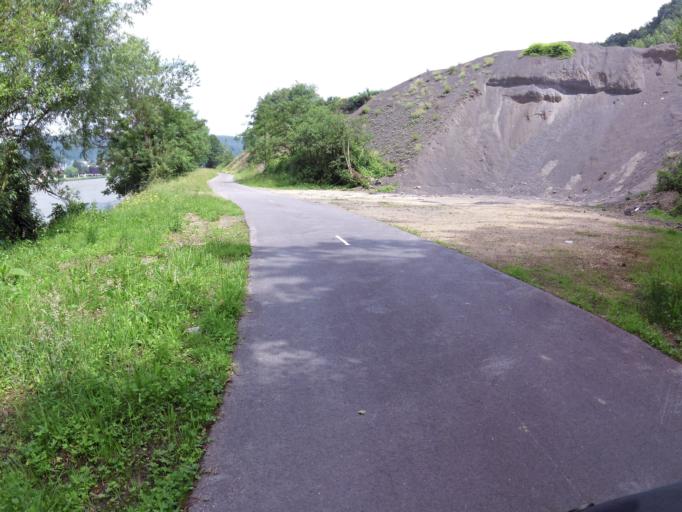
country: FR
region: Champagne-Ardenne
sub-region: Departement des Ardennes
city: Vireux-Wallerand
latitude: 50.1040
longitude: 4.7670
